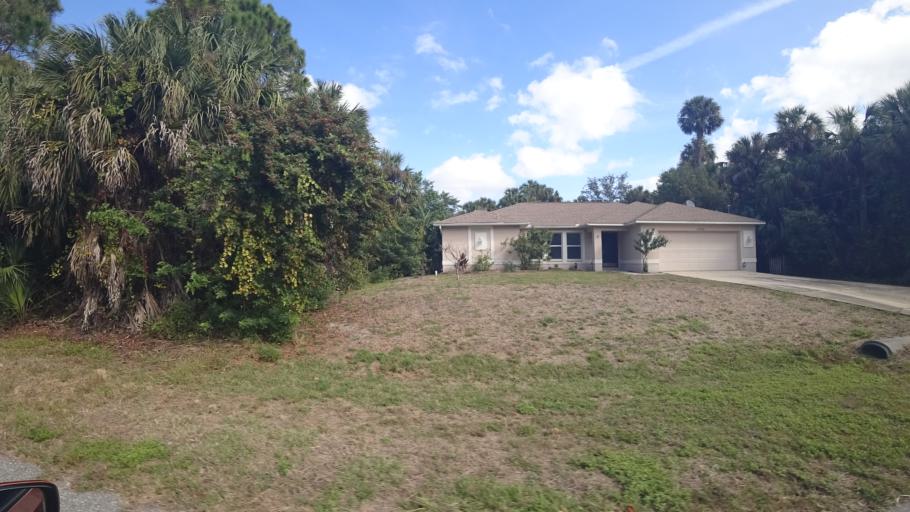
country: US
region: Florida
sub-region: Charlotte County
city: Port Charlotte
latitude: 27.0467
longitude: -82.1304
